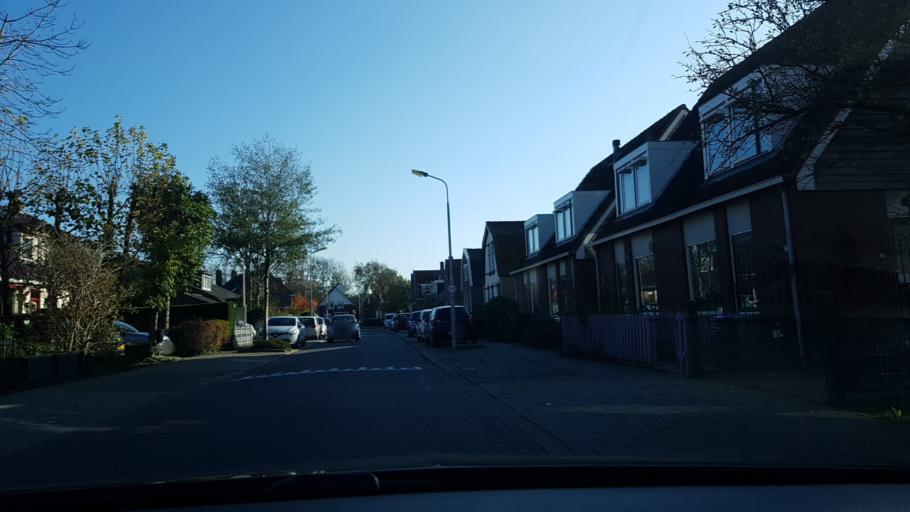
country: NL
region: North Holland
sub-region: Gemeente Uitgeest
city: Uitgeest
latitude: 52.4637
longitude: 4.7368
